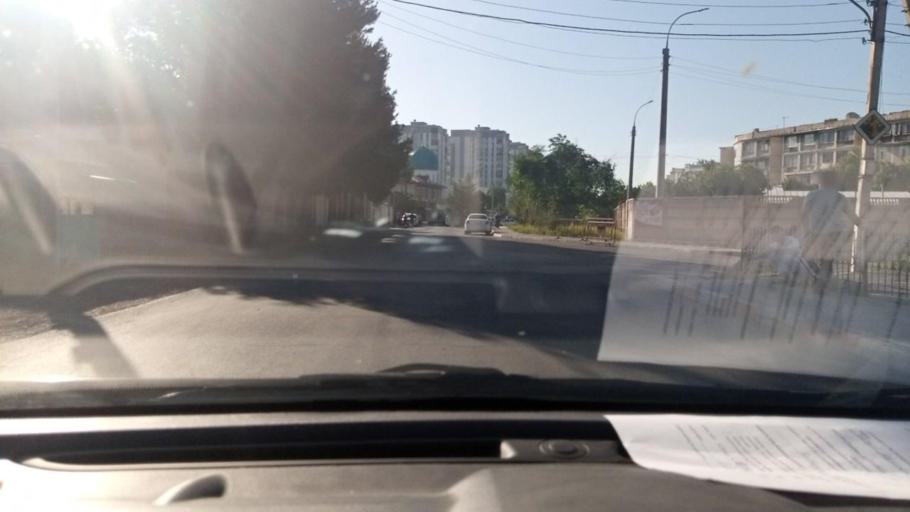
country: UZ
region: Toshkent
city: Salor
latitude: 41.3245
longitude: 69.3553
